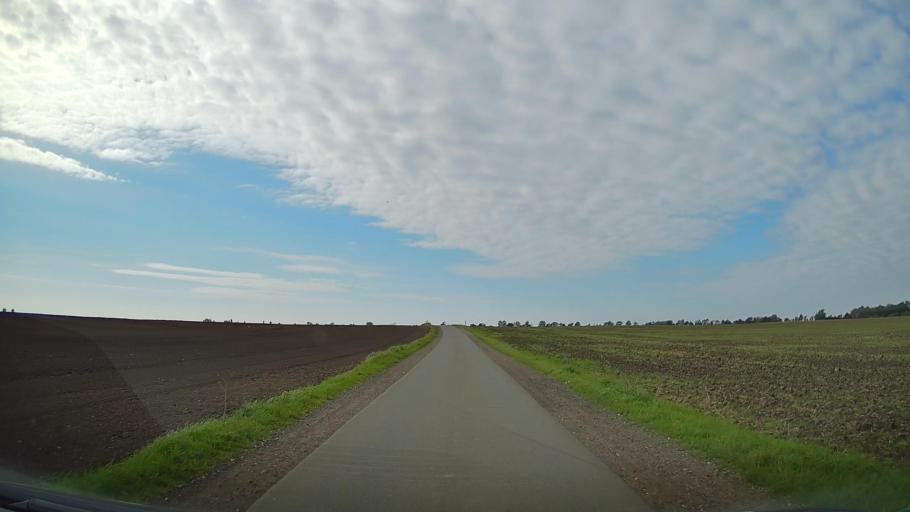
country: DE
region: Schleswig-Holstein
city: Grossenbrode
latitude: 54.4968
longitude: 11.0516
